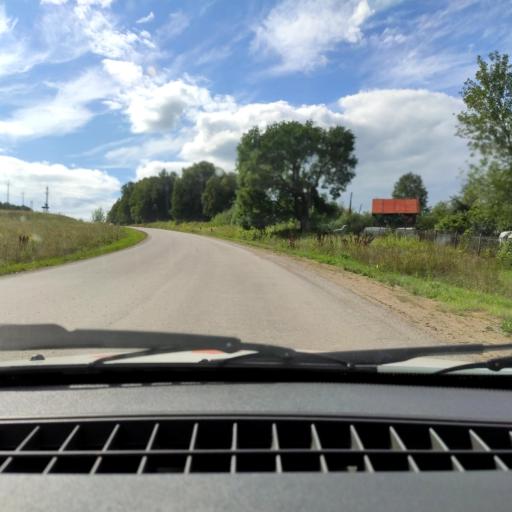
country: RU
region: Bashkortostan
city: Kudeyevskiy
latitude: 54.8845
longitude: 56.6244
